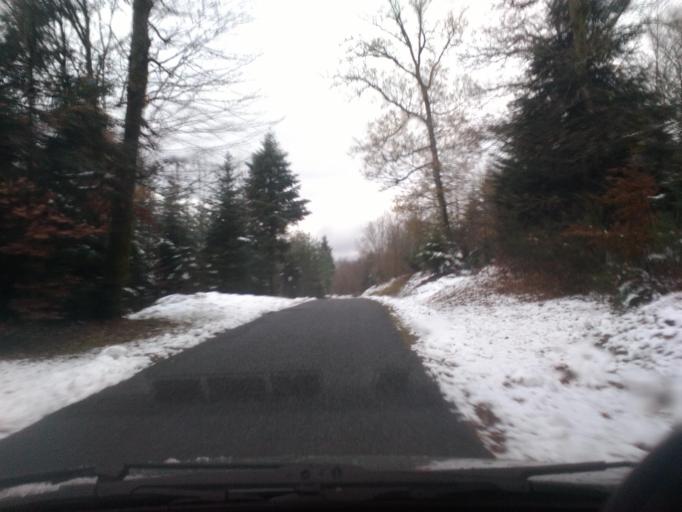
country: FR
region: Lorraine
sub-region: Departement des Vosges
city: Sainte-Marguerite
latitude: 48.2922
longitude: 7.0259
